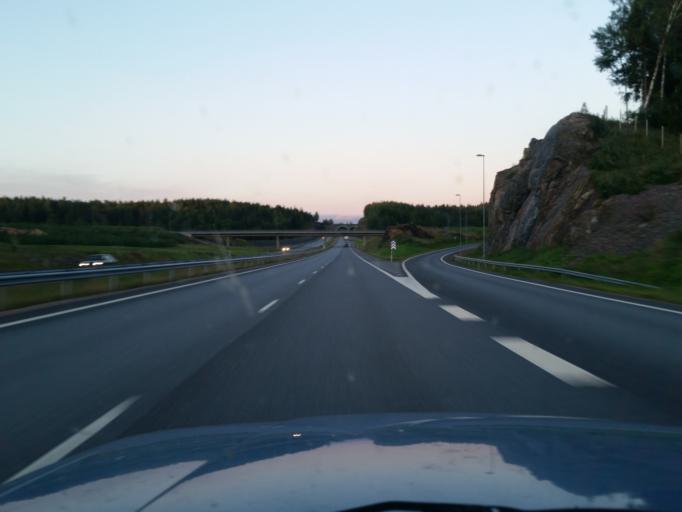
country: FI
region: Uusimaa
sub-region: Helsinki
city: Sammatti
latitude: 60.3786
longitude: 23.7993
